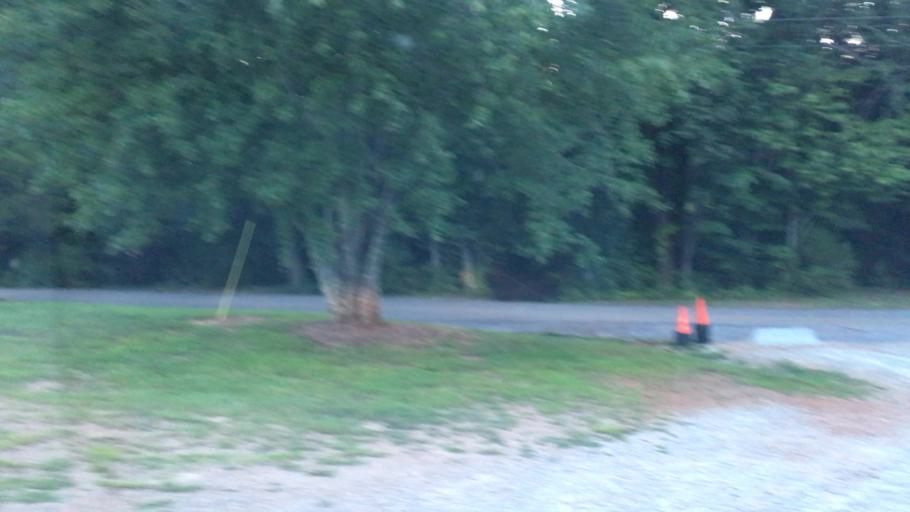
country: US
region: Georgia
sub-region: Jackson County
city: Braselton
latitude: 34.1446
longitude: -83.8137
